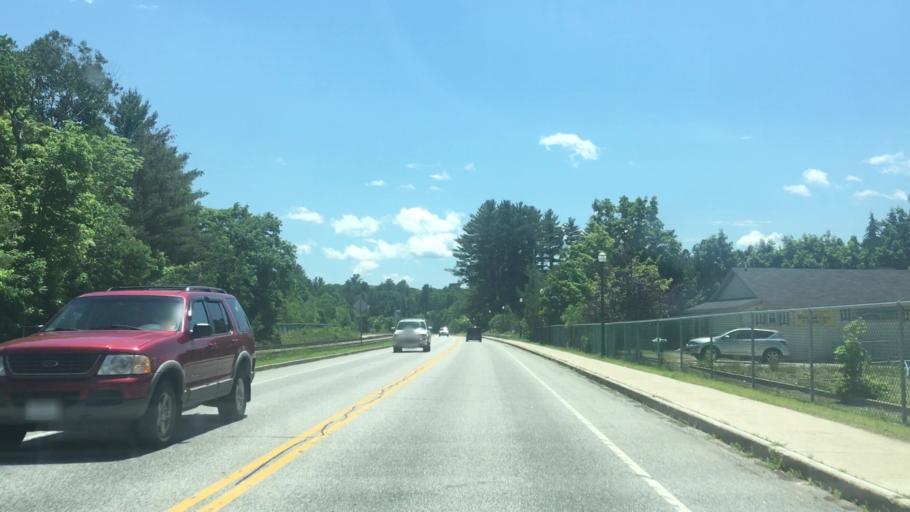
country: US
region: New Hampshire
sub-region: Carroll County
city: North Conway
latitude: 44.0499
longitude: -71.1236
